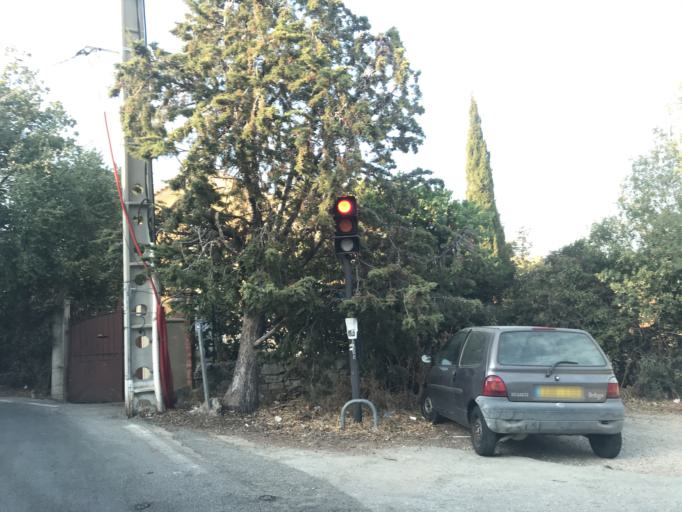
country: FR
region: Provence-Alpes-Cote d'Azur
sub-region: Departement du Var
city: La Seyne-sur-Mer
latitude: 43.0852
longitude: 5.8861
